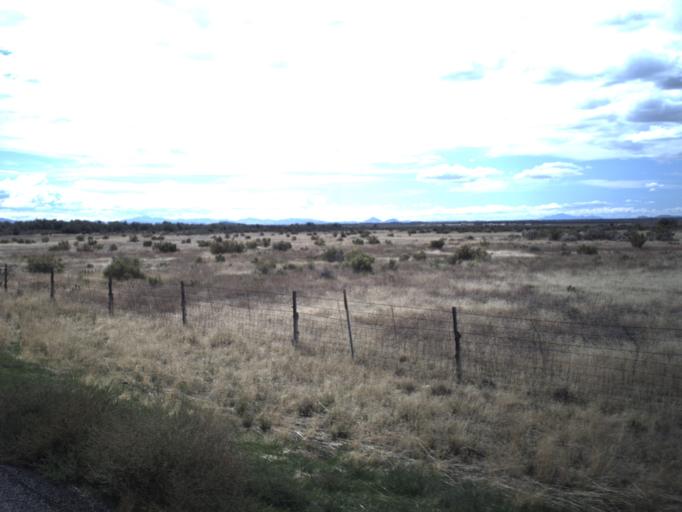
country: US
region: Utah
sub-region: Millard County
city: Fillmore
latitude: 39.0949
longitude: -112.4100
